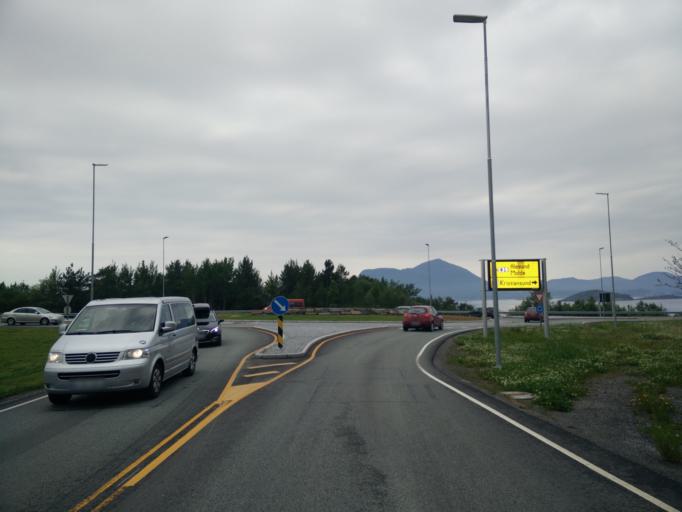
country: NO
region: More og Romsdal
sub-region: Kristiansund
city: Rensvik
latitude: 62.9754
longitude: 7.7882
